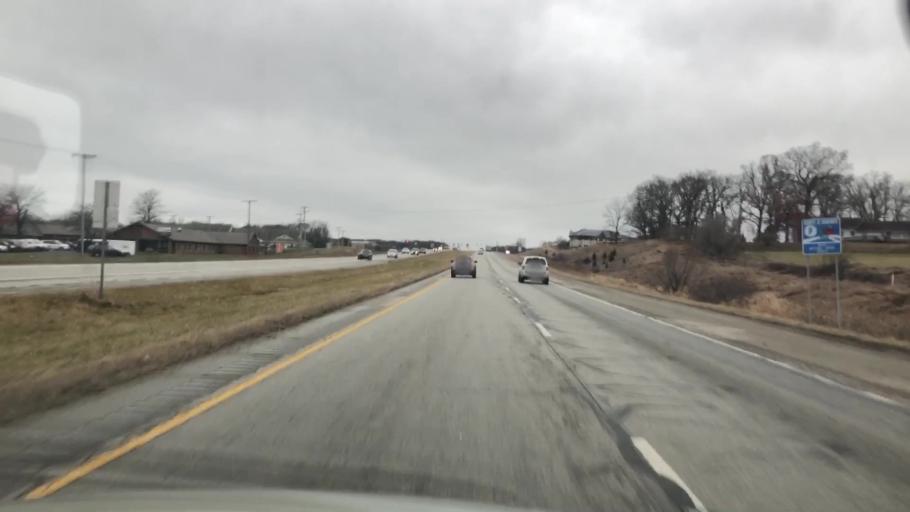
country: US
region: Indiana
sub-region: Kosciusko County
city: Winona Lake
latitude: 41.2475
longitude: -85.8236
